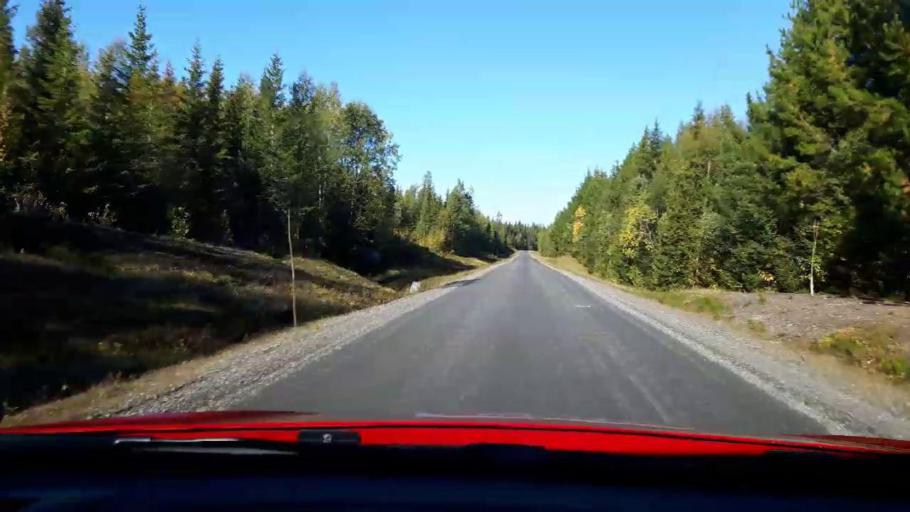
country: NO
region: Nord-Trondelag
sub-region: Lierne
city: Sandvika
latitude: 64.5284
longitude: 14.0502
